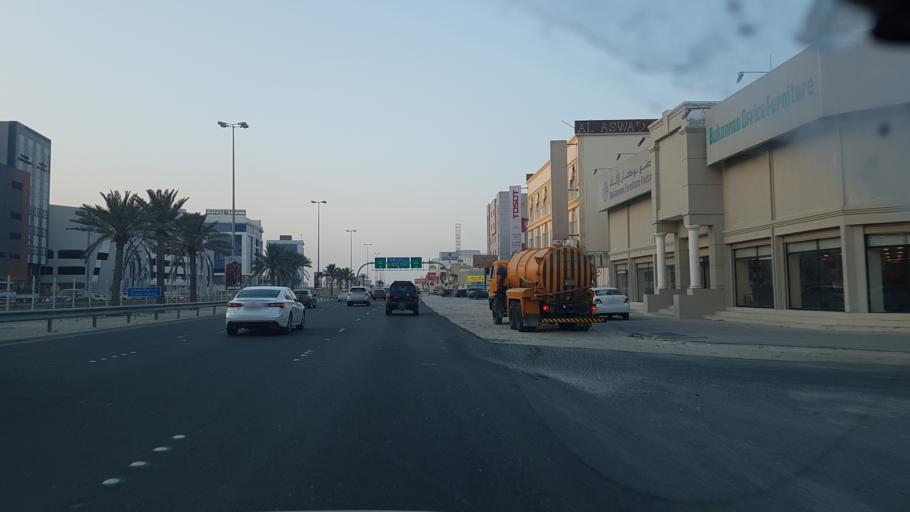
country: BH
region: Northern
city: Ar Rifa'
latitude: 26.1340
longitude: 50.5852
